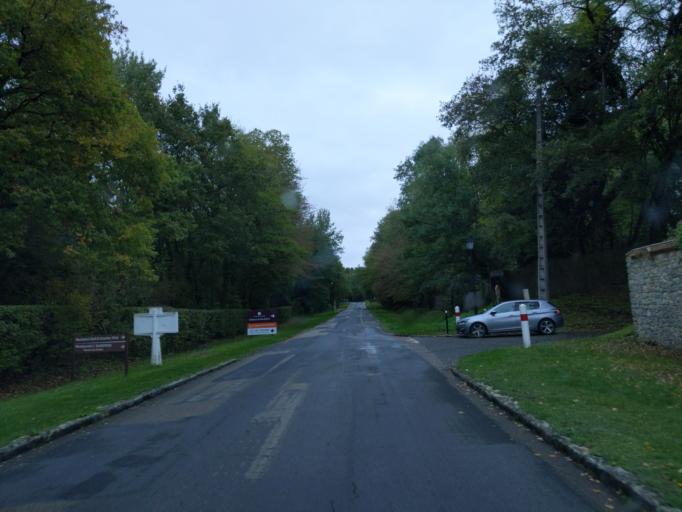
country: FR
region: Ile-de-France
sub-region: Departement des Yvelines
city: Bullion
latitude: 48.5894
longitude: 1.9904
